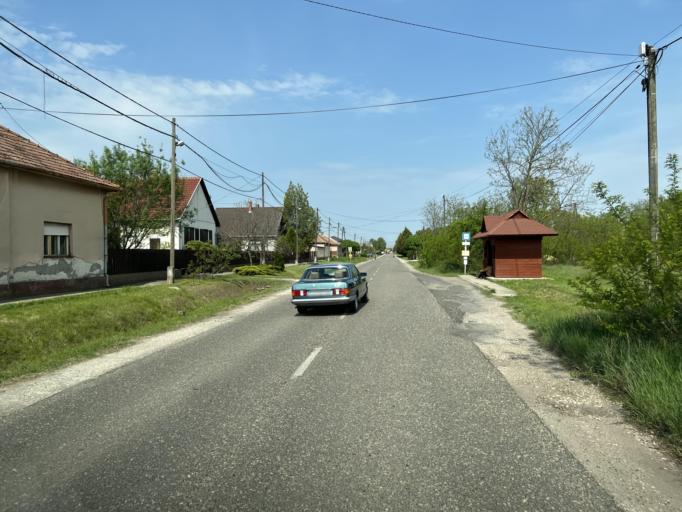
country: HU
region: Pest
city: Tortel
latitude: 47.1195
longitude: 19.9447
